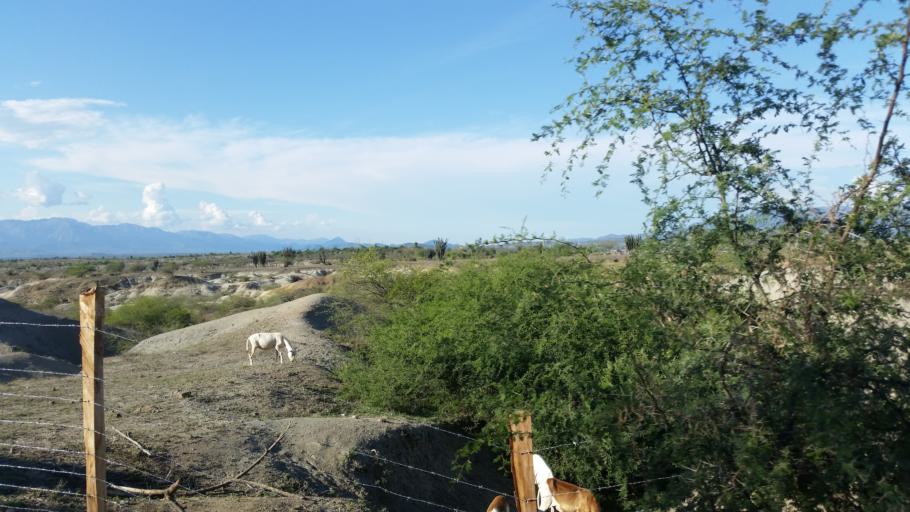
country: CO
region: Huila
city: Villavieja
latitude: 3.2322
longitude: -75.1570
